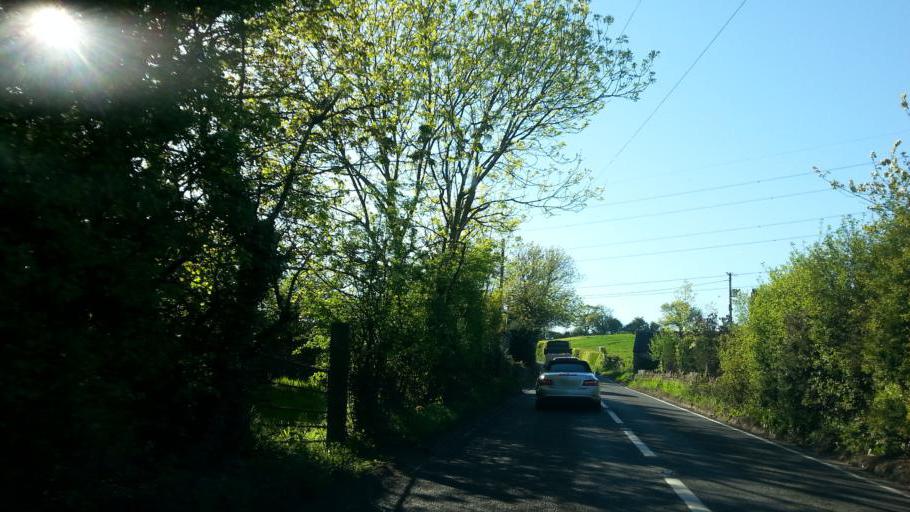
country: GB
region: England
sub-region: Somerset
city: Evercreech
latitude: 51.1638
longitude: -2.5269
